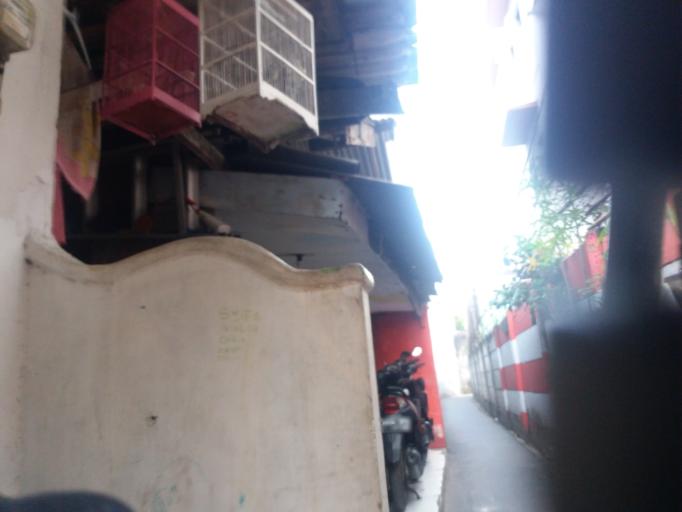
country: ID
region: Jakarta Raya
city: Jakarta
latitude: -6.2202
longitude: 106.8263
